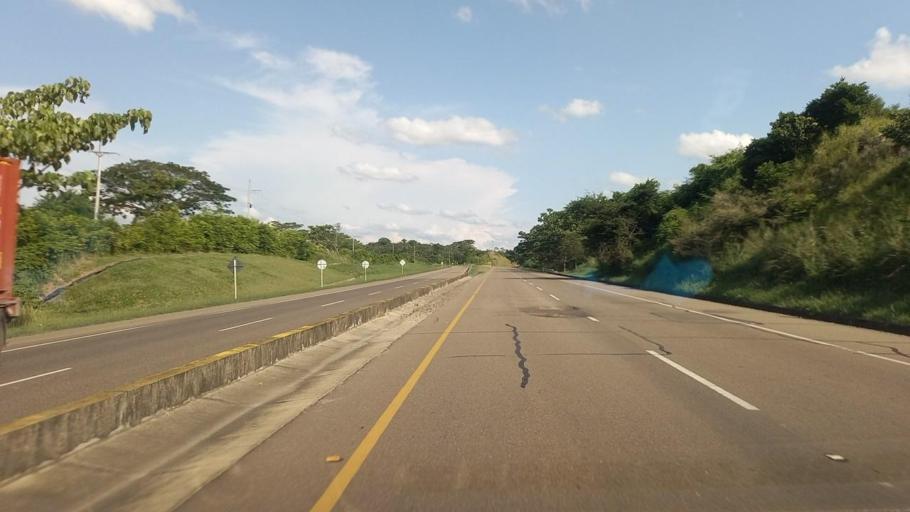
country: CO
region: Boyaca
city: Puerto Boyaca
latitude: 6.1472
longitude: -74.5630
